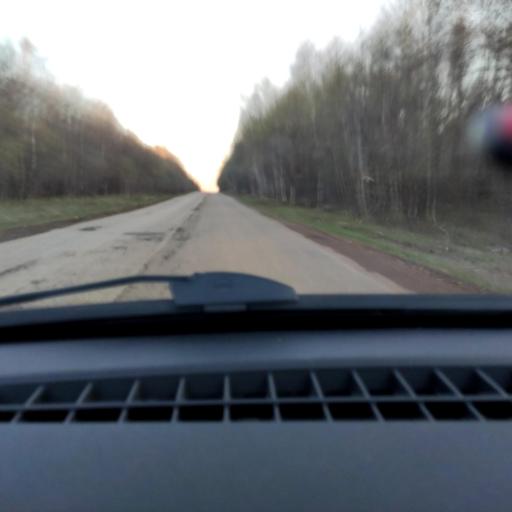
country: RU
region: Bashkortostan
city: Chishmy
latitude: 54.4498
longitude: 55.5492
